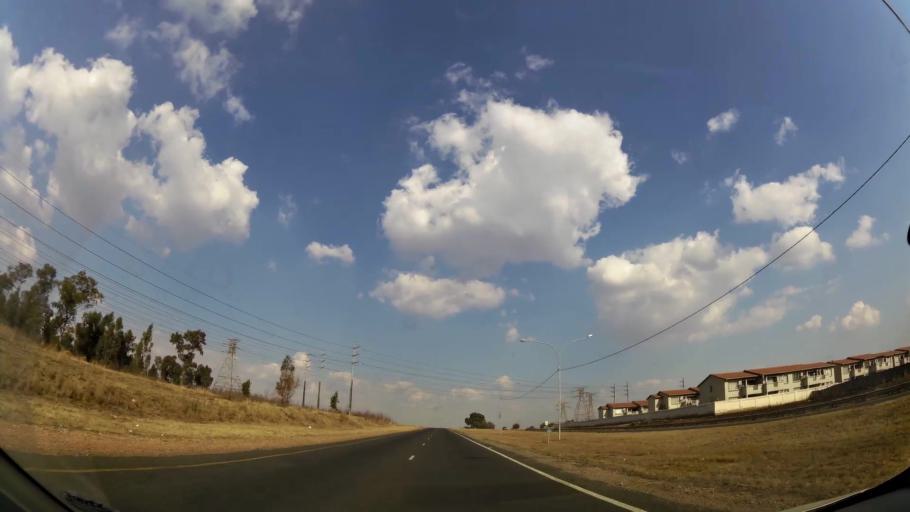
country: ZA
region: Gauteng
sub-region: Ekurhuleni Metropolitan Municipality
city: Brakpan
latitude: -26.2750
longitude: 28.3281
